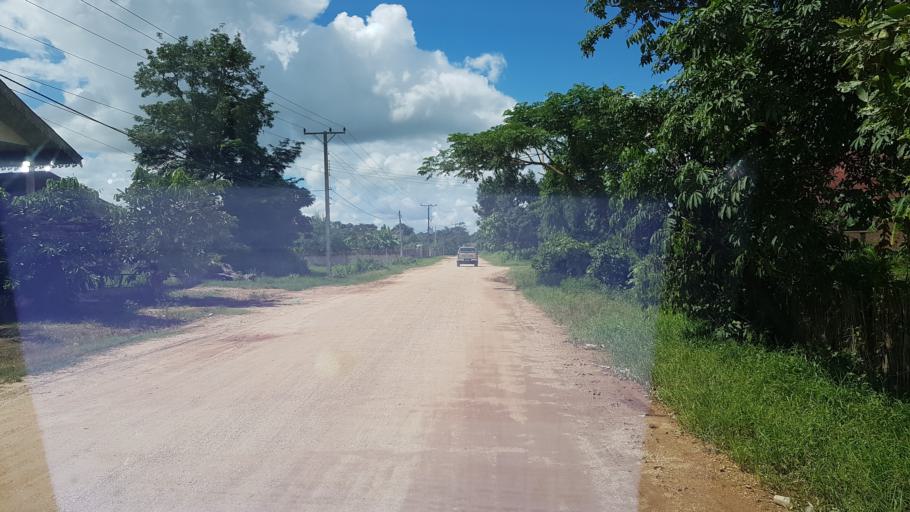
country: LA
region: Vientiane
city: Vientiane
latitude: 18.2176
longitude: 102.5163
